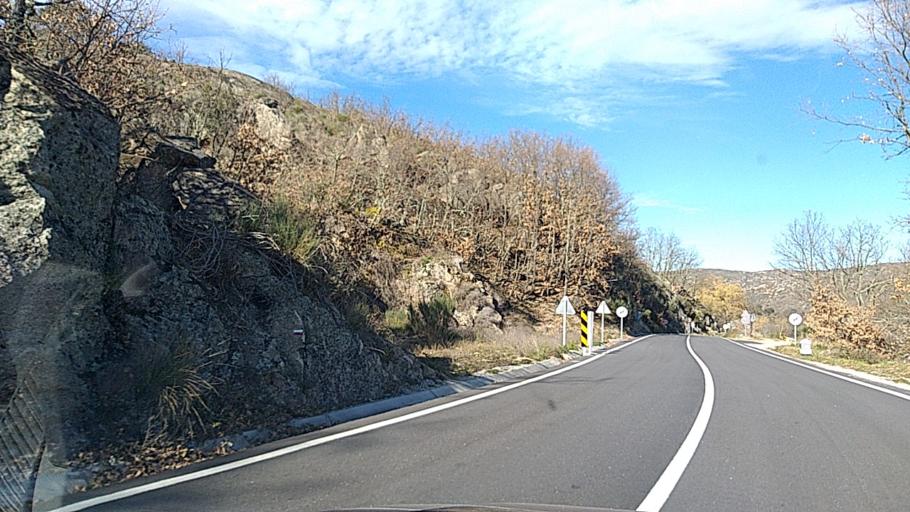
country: ES
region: Castille and Leon
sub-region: Provincia de Salamanca
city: Fuentes de Onoro
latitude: 40.6147
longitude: -6.9204
